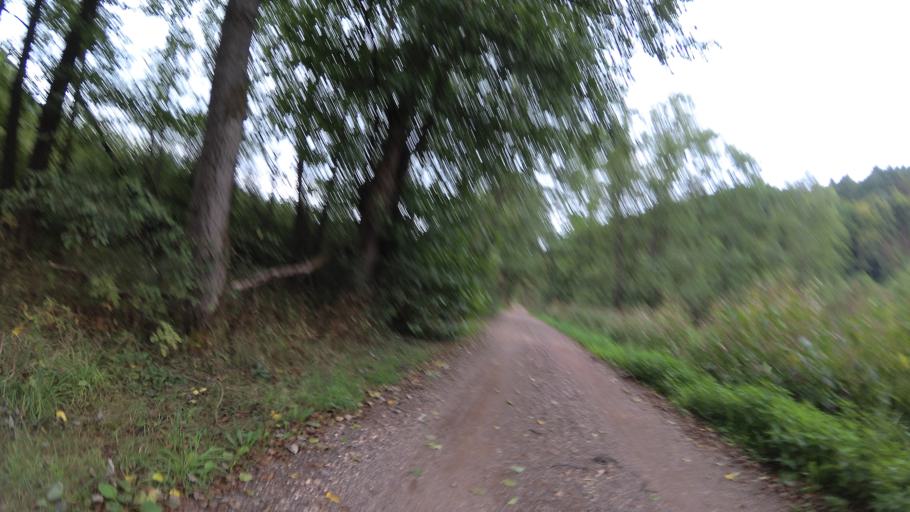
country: DE
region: Saarland
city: Wadern
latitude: 49.5172
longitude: 6.8854
